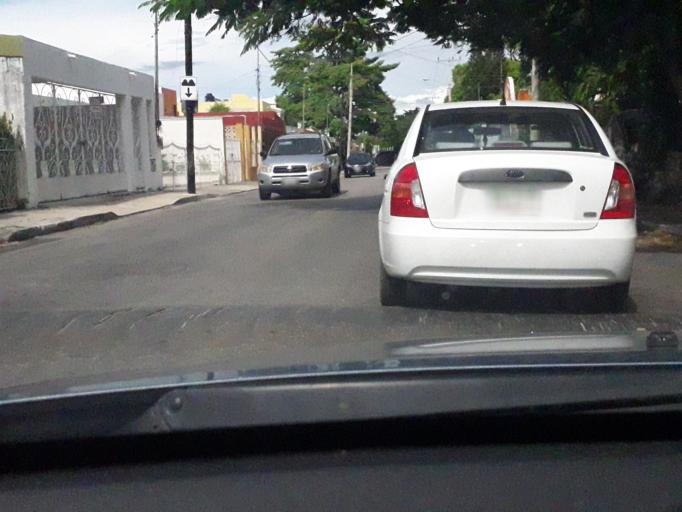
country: MX
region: Yucatan
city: Merida
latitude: 20.9786
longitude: -89.6553
